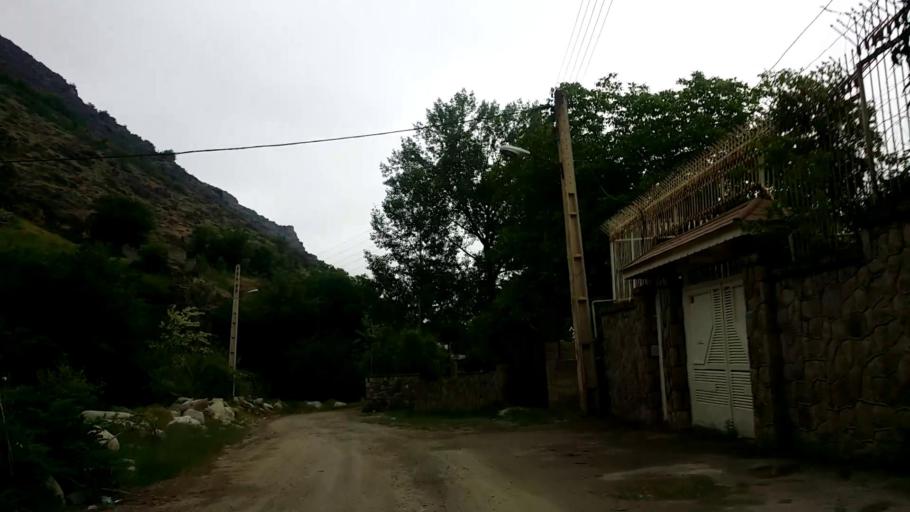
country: IR
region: Mazandaran
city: `Abbasabad
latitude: 36.4961
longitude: 51.1373
